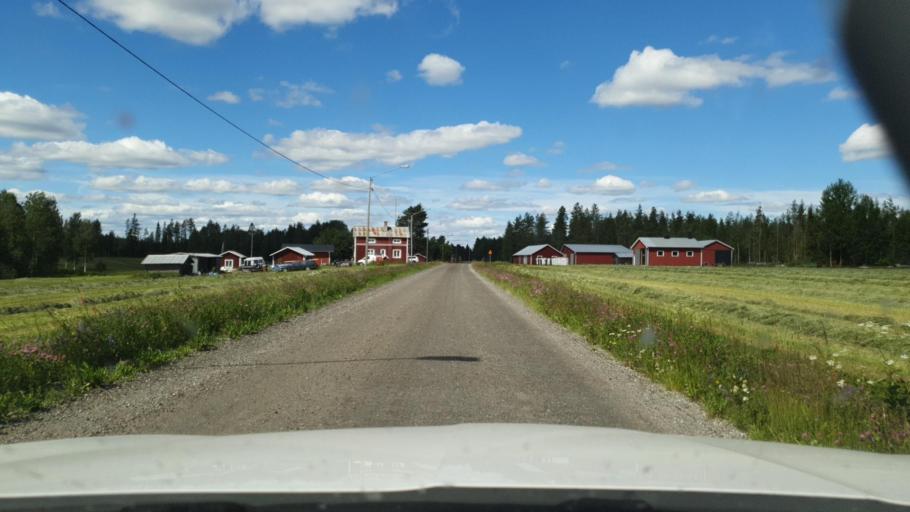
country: SE
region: Vaesterbotten
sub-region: Skelleftea Kommun
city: Backa
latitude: 65.1832
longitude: 21.0672
